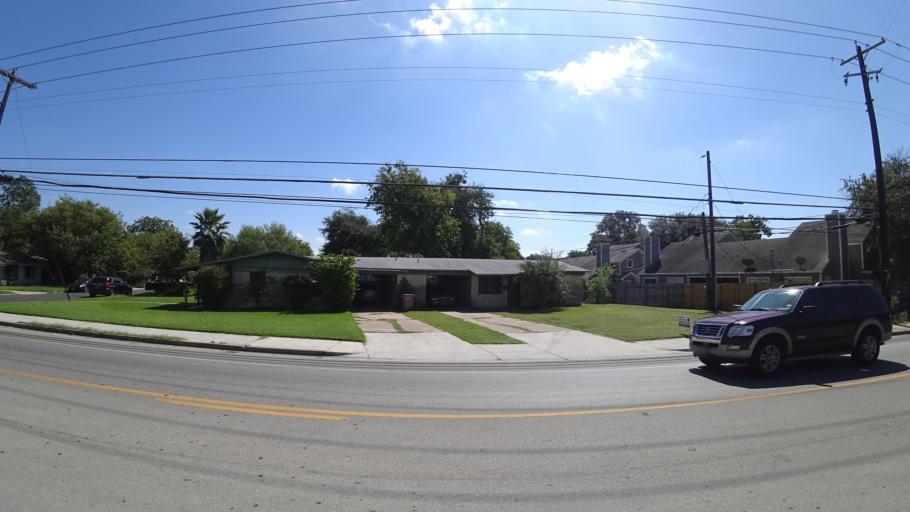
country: US
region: Texas
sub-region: Travis County
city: Austin
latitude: 30.3167
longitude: -97.7004
